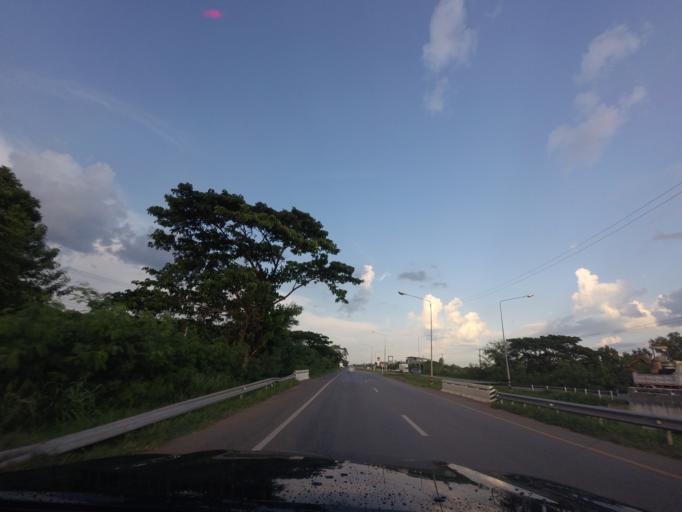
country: TH
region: Khon Kaen
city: Khon Kaen
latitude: 16.3986
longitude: 102.8649
